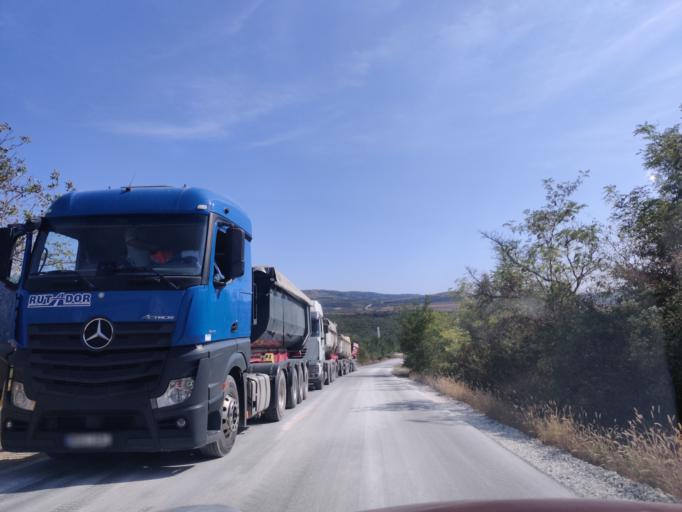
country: MD
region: Ungheni
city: Ungheni
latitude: 47.2577
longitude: 27.9932
